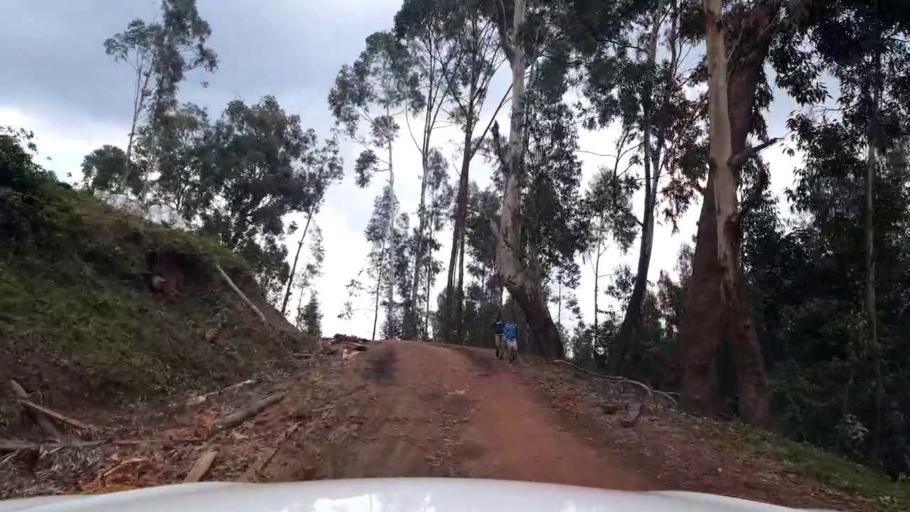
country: UG
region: Western Region
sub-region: Kisoro District
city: Kisoro
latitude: -1.3854
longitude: 29.7985
